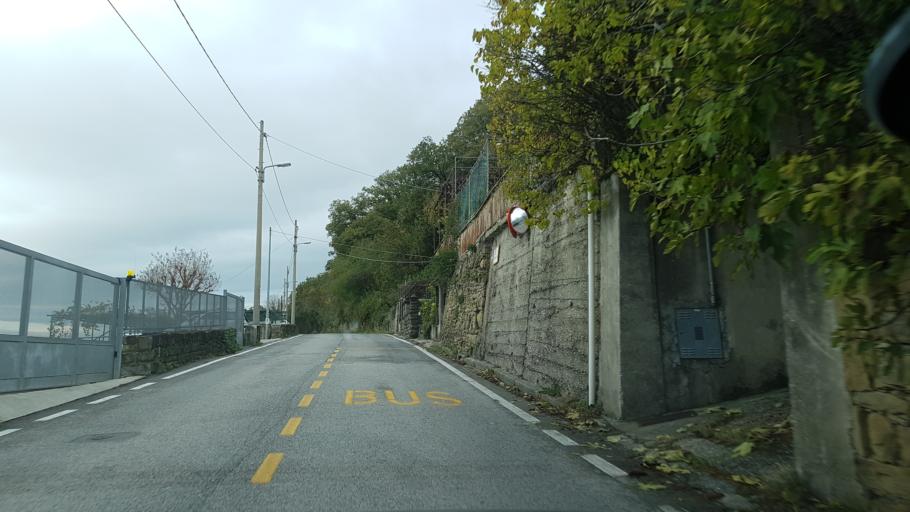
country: IT
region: Friuli Venezia Giulia
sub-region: Provincia di Trieste
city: Prosecco-Contovello
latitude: 45.6893
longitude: 13.7495
